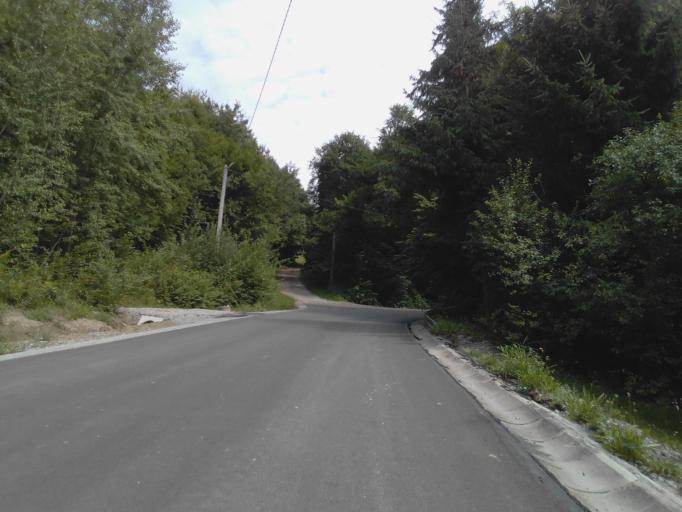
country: PL
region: Subcarpathian Voivodeship
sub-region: Powiat jasielski
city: Tarnowiec
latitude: 49.7726
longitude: 21.5674
